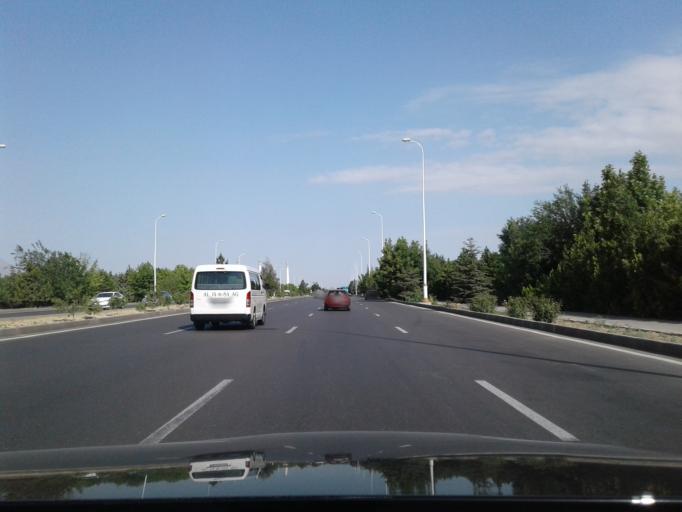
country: TM
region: Ahal
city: Abadan
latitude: 38.0134
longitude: 58.2697
